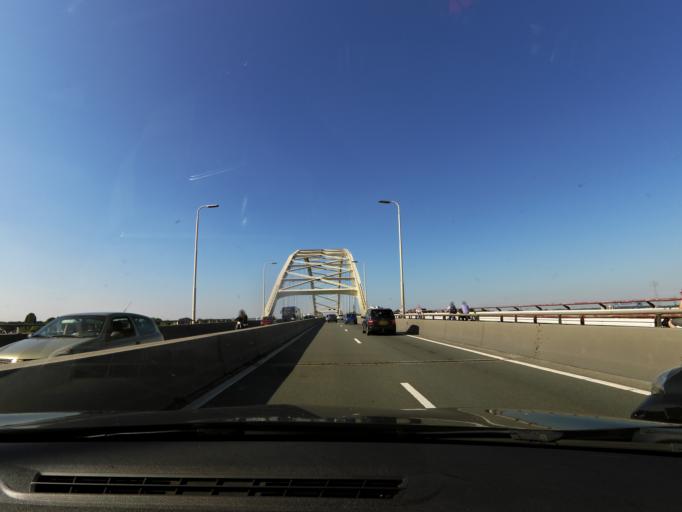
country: NL
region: South Holland
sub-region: Gemeente Papendrecht
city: Papendrecht
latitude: 51.8215
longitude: 4.7061
